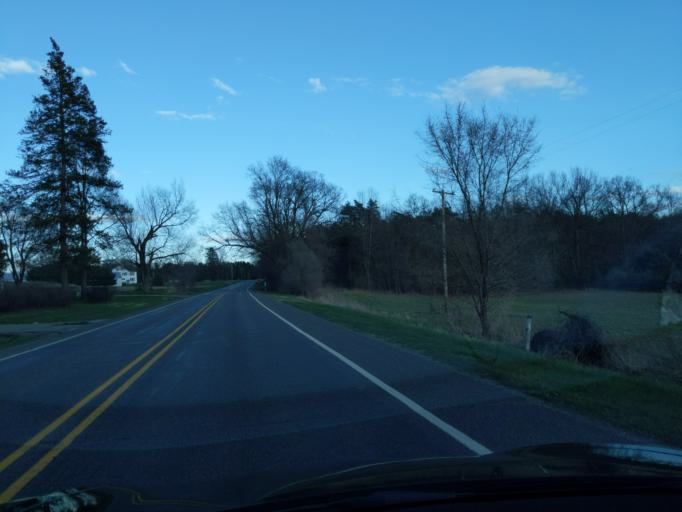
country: US
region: Michigan
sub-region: Ingham County
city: Mason
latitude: 42.5500
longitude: -84.3799
